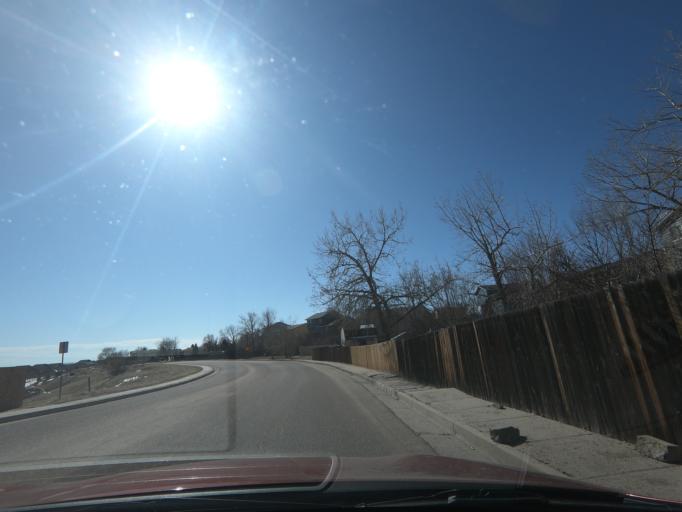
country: US
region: Colorado
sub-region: El Paso County
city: Security-Widefield
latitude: 38.7216
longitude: -104.6899
